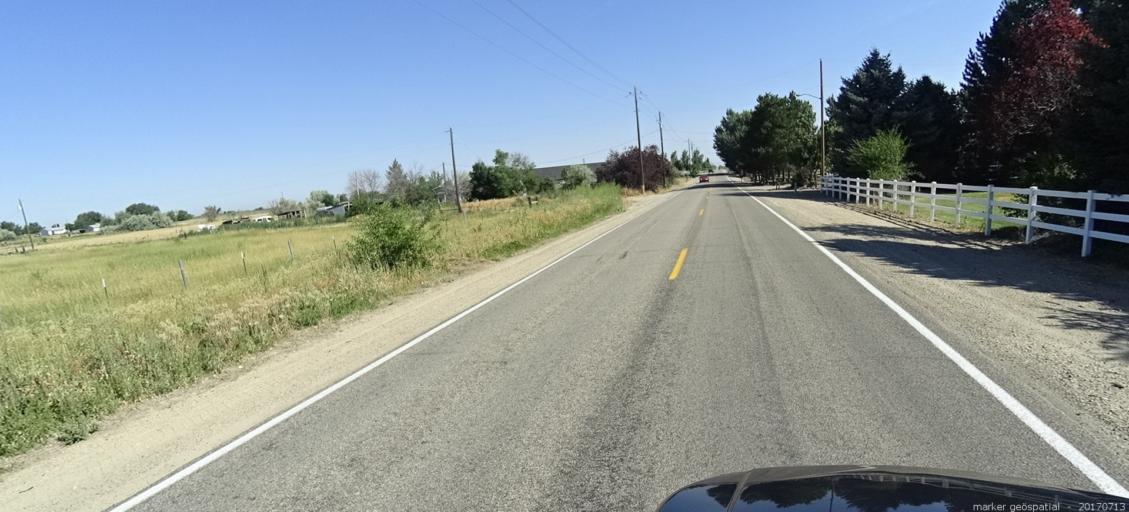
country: US
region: Idaho
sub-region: Ada County
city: Kuna
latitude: 43.5232
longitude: -116.4138
